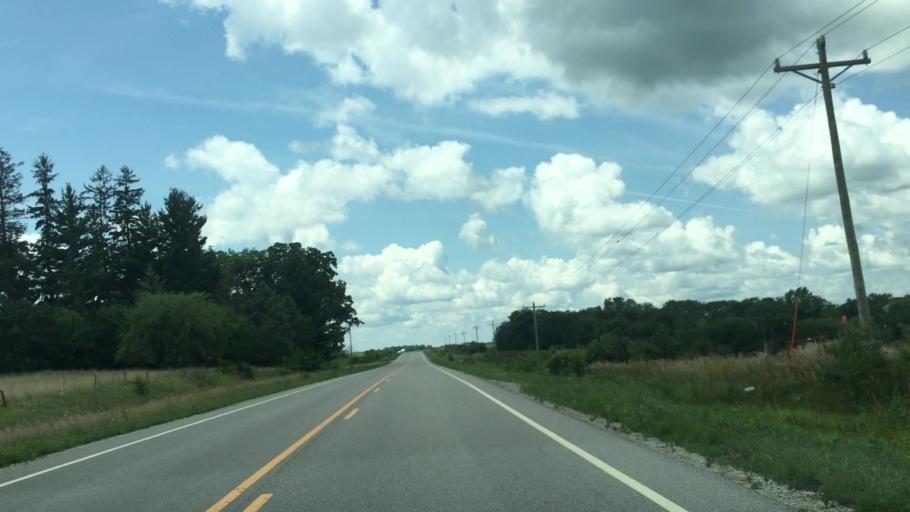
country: US
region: Iowa
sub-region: Johnson County
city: Solon
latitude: 41.8356
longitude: -91.4353
